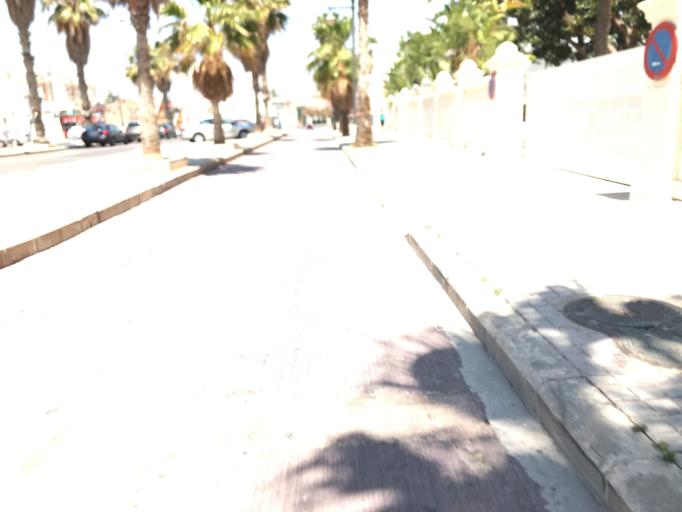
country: ES
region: Valencia
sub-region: Provincia de Valencia
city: Alboraya
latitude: 39.4666
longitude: -0.3249
